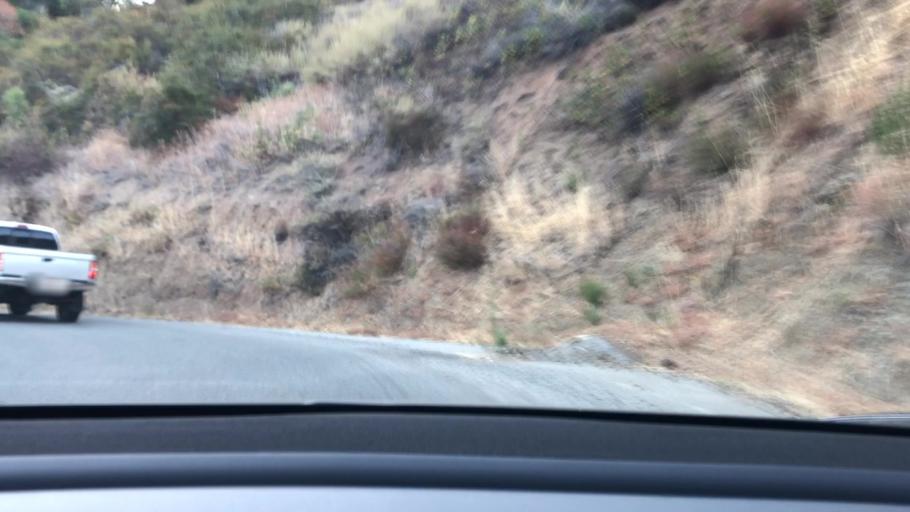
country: US
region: California
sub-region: Santa Clara County
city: Saratoga
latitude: 37.2557
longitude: -122.0587
